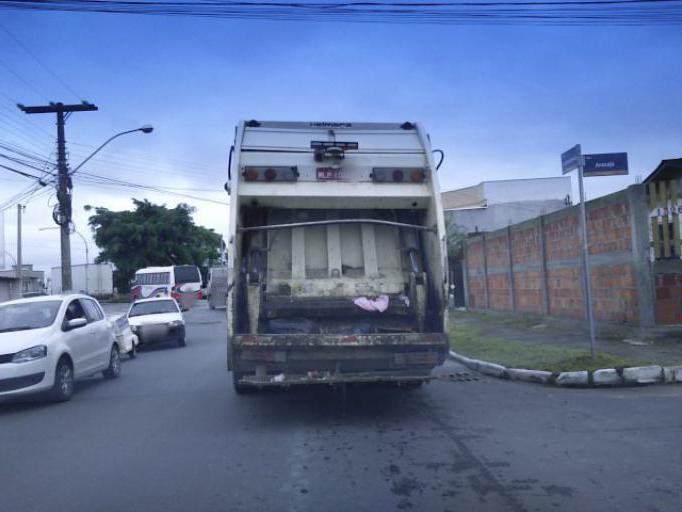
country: BR
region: Santa Catarina
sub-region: Itajai
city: Itajai
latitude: -26.8999
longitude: -48.7009
